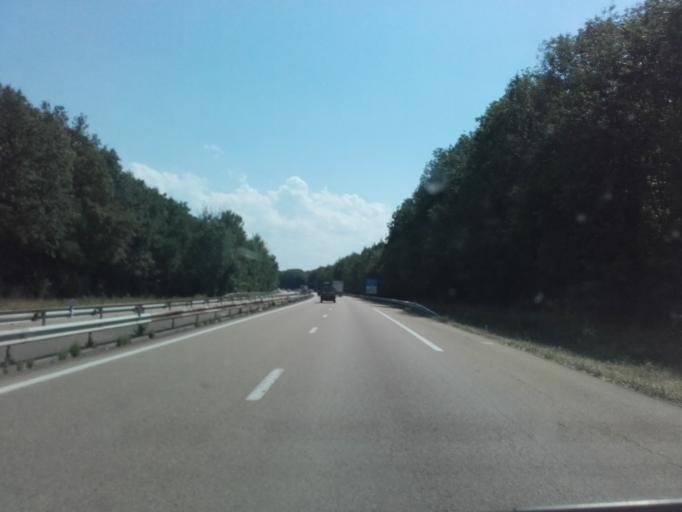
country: FR
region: Bourgogne
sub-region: Departement de l'Yonne
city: Joux-la-Ville
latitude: 47.6040
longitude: 3.9095
